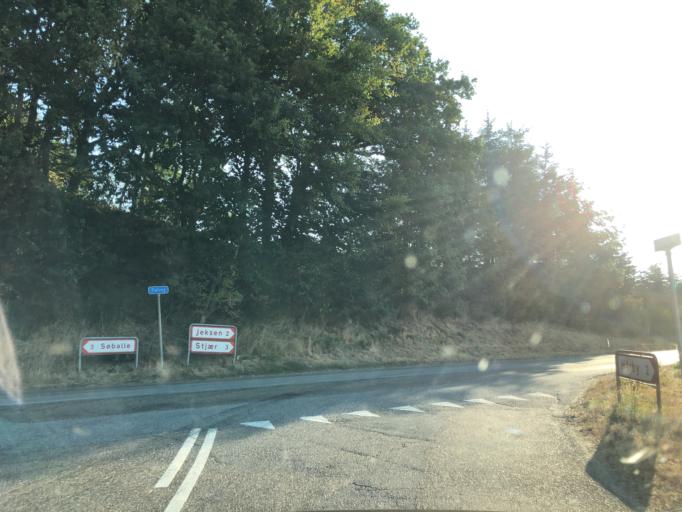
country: DK
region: Central Jutland
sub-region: Skanderborg Kommune
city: Skanderborg
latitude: 56.0966
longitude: 9.9394
